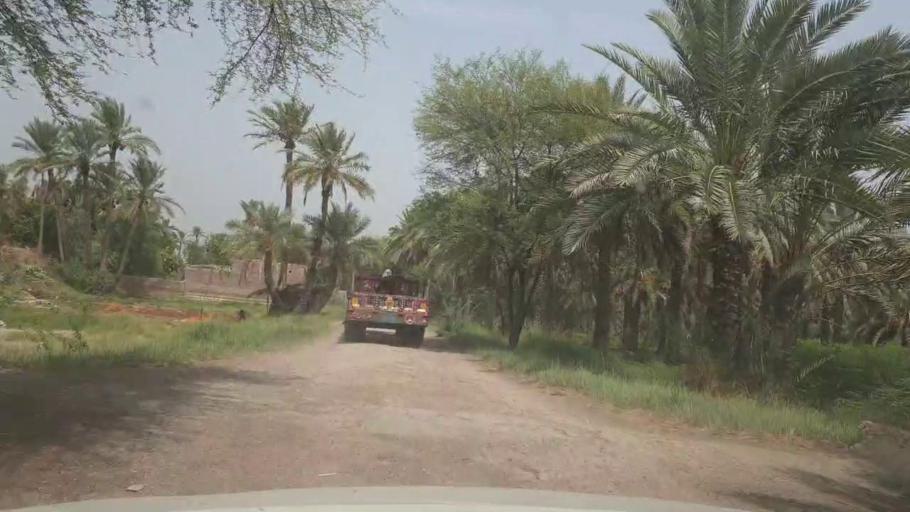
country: PK
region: Sindh
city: Kot Diji
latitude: 27.3500
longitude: 68.7043
